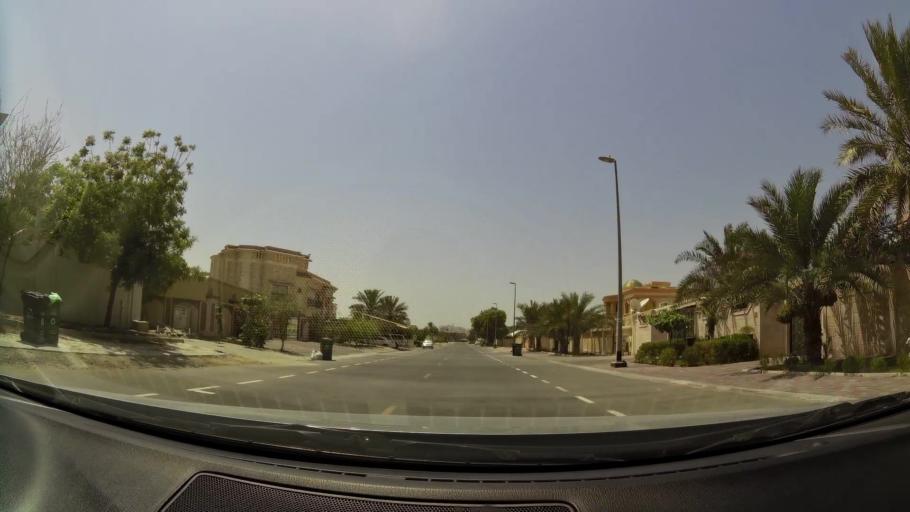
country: AE
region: Dubai
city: Dubai
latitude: 25.0995
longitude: 55.2174
